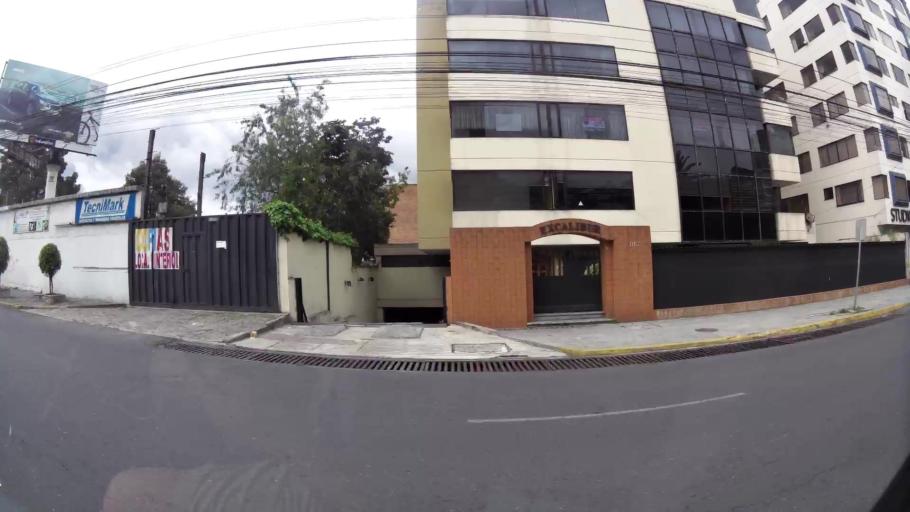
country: EC
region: Pichincha
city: Quito
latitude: -0.1637
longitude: -78.4894
